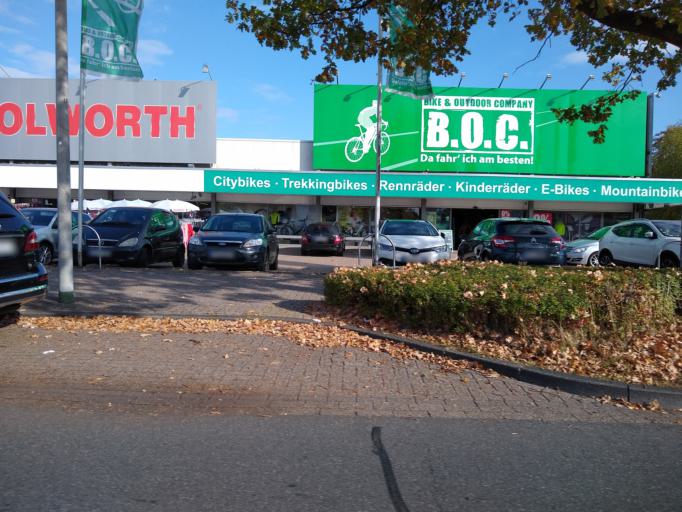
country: DE
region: Lower Saxony
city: Oldenburg
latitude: 53.1602
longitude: 8.1716
